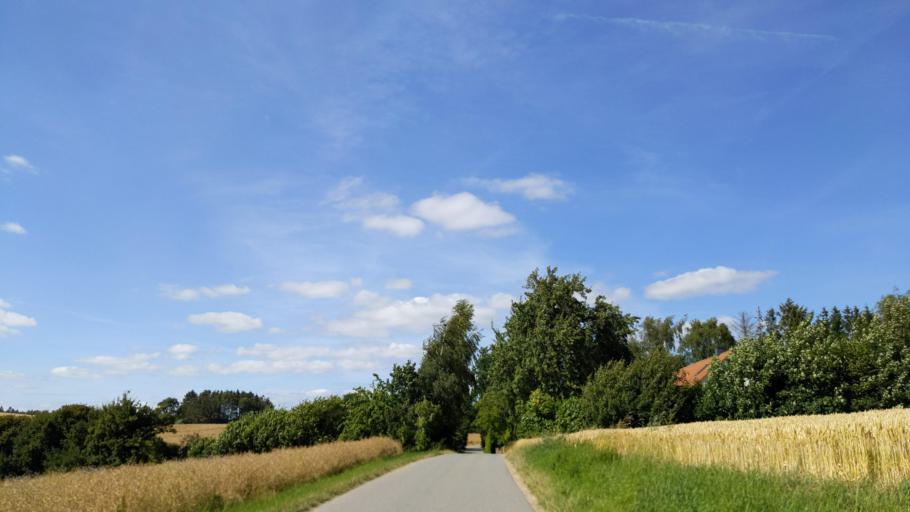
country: DE
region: Schleswig-Holstein
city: Kasseedorf
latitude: 54.1395
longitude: 10.7372
